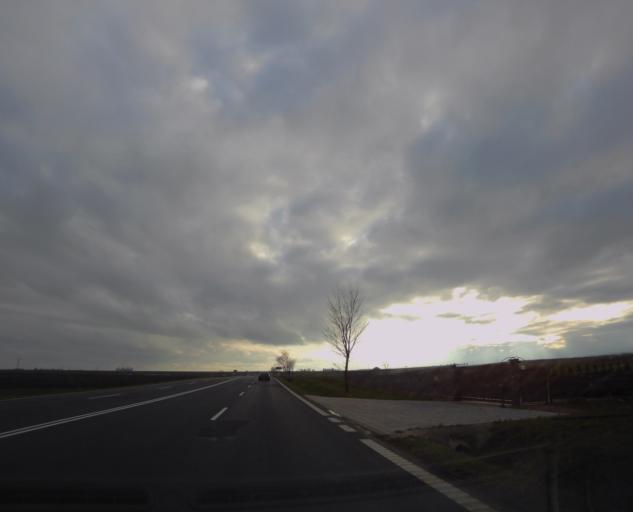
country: PL
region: Subcarpathian Voivodeship
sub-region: Powiat jaroslawski
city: Radymno
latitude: 49.9181
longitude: 22.8197
